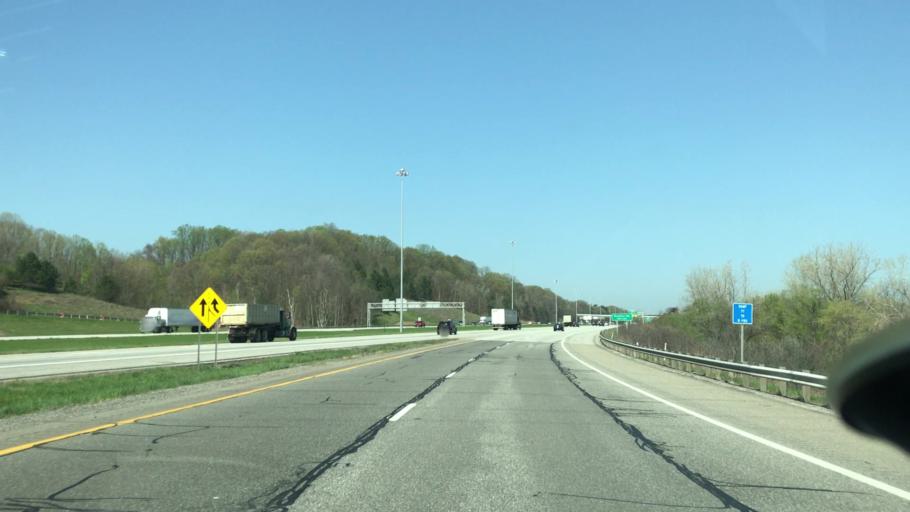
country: US
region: Ohio
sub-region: Cuyahoga County
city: Seven Hills
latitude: 41.4086
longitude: -81.6518
